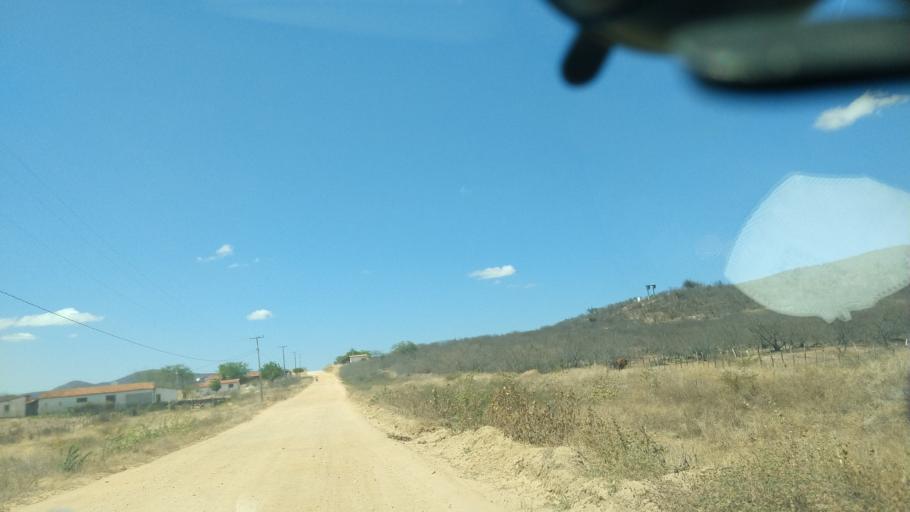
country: BR
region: Rio Grande do Norte
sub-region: Sao Tome
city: Sao Tome
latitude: -5.9801
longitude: -36.1751
